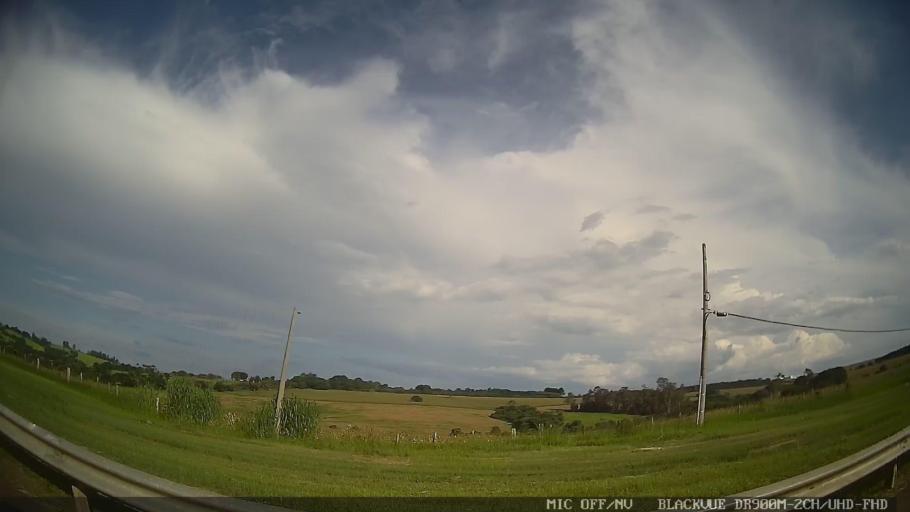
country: BR
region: Sao Paulo
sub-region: Tiete
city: Tiete
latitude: -23.1182
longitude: -47.6998
